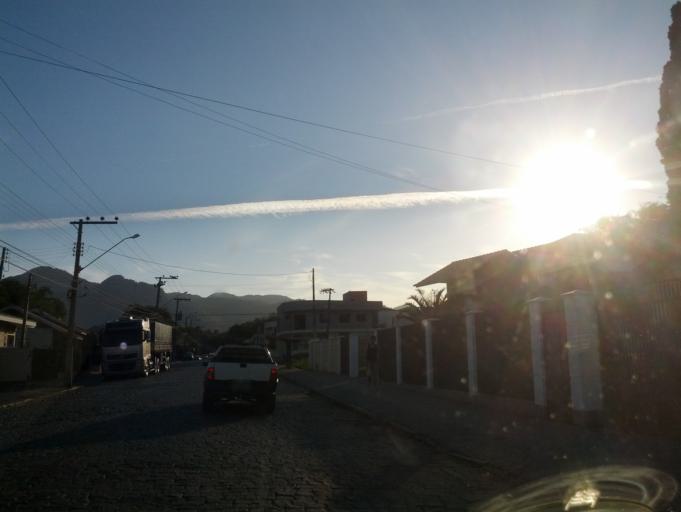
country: BR
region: Santa Catarina
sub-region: Indaial
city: Indaial
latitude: -26.8985
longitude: -49.2509
